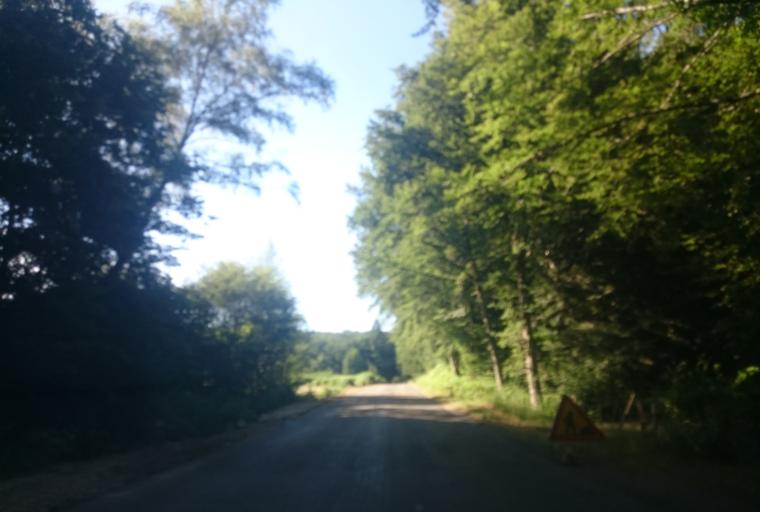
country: FR
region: Auvergne
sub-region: Departement du Cantal
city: Laroquebrou
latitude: 44.9238
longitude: 2.1937
